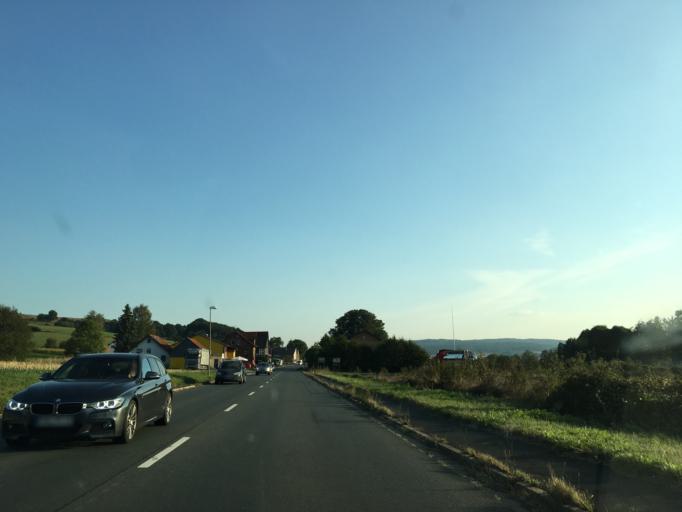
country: DE
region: Hesse
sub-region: Regierungsbezirk Giessen
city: Munchhausen
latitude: 50.9384
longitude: 8.7053
